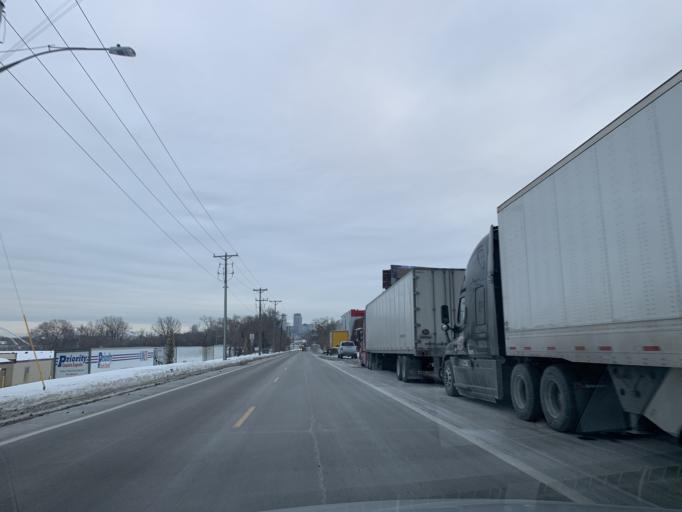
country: US
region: Minnesota
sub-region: Anoka County
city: Columbia Heights
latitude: 45.0196
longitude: -93.2817
